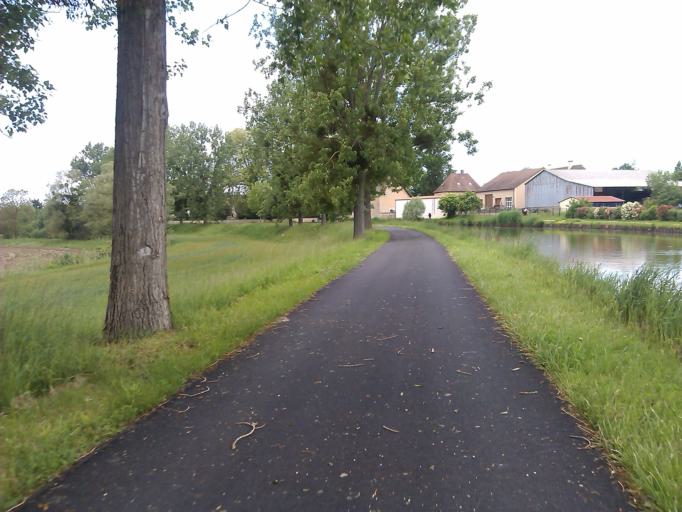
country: FR
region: Bourgogne
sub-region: Departement de Saone-et-Loire
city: Virey-le-Grand
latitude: 46.8317
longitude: 4.8480
